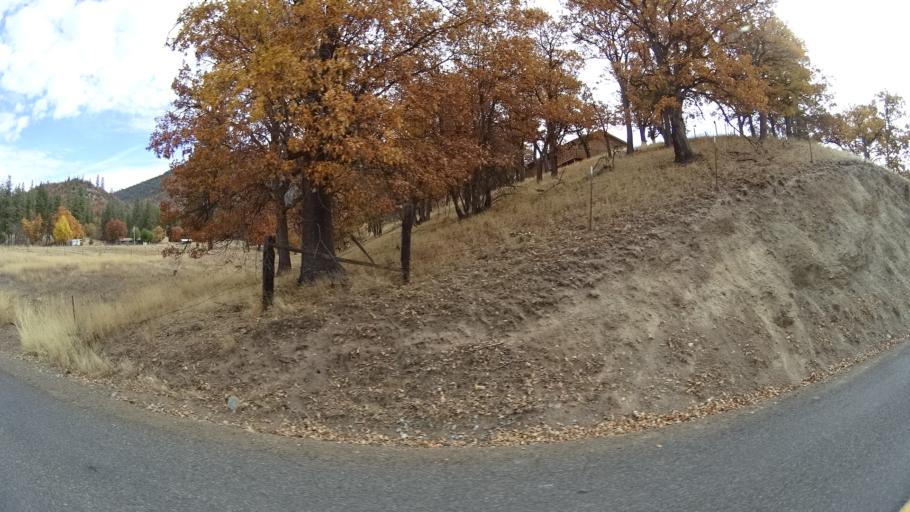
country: US
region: California
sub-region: Siskiyou County
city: Yreka
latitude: 41.6483
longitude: -122.8317
